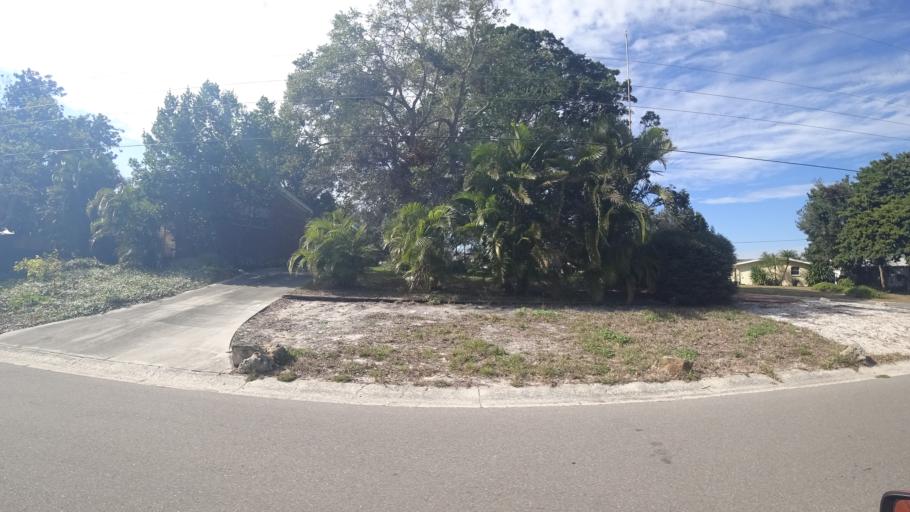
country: US
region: Florida
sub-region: Manatee County
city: West Bradenton
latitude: 27.5166
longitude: -82.6334
